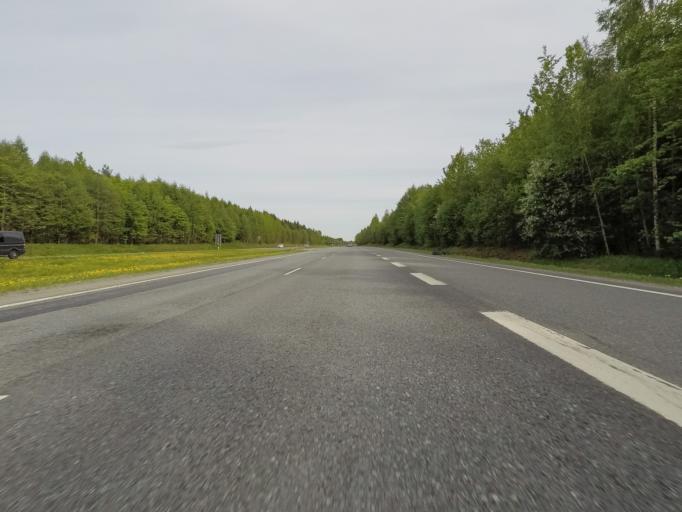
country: FI
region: Haeme
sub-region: Haemeenlinna
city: Kalvola
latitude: 61.0956
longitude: 24.1728
